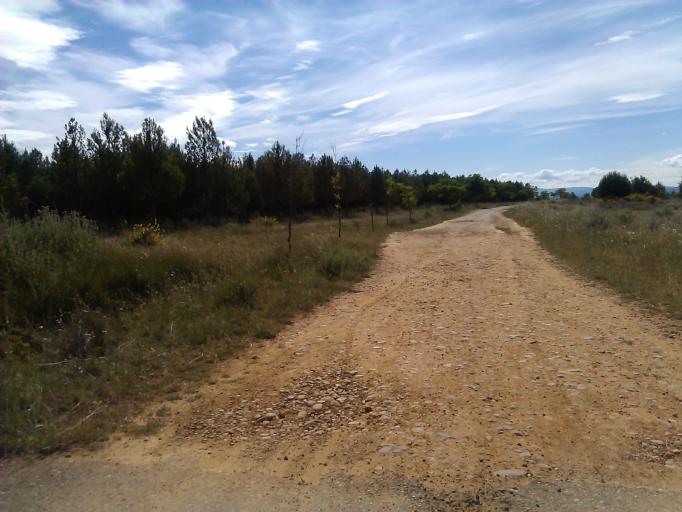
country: ES
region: Castille and Leon
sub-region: Provincia de Leon
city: San Justo de la Vega
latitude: 42.4533
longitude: -5.9947
